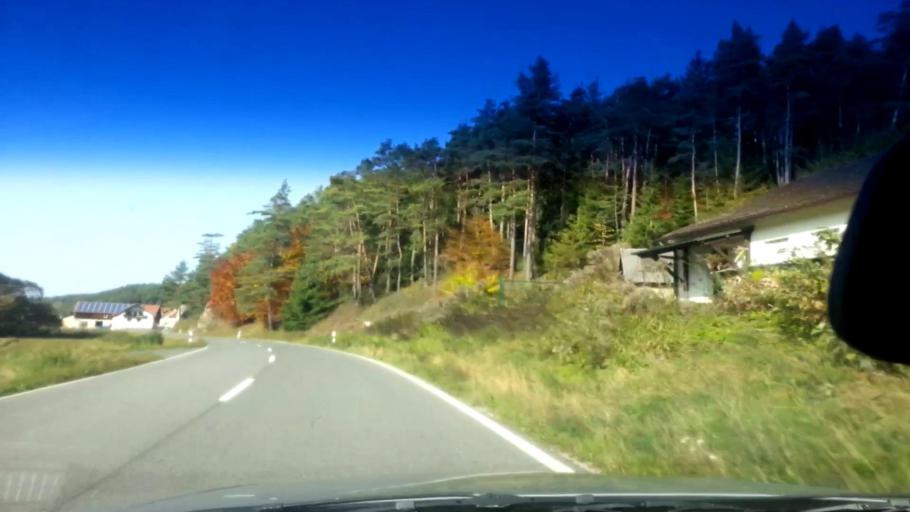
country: DE
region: Bavaria
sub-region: Upper Franconia
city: Stadelhofen
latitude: 49.9626
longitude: 11.2049
